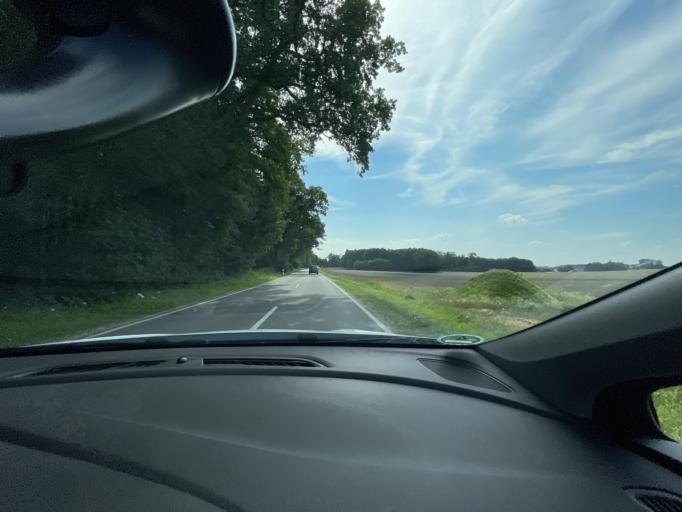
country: DE
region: Bavaria
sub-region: Upper Bavaria
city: Rohrmoos
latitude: 48.3117
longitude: 11.4041
